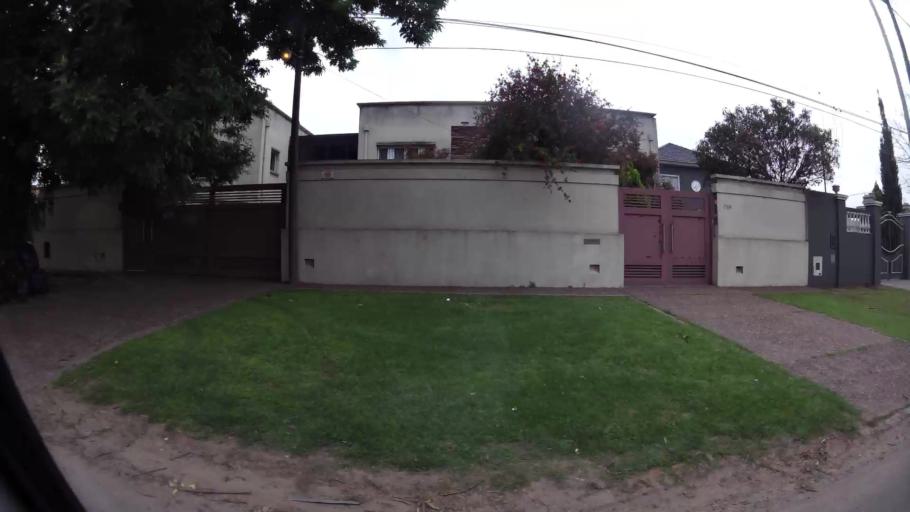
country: AR
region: Buenos Aires
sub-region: Partido de La Plata
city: La Plata
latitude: -34.9218
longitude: -57.9933
